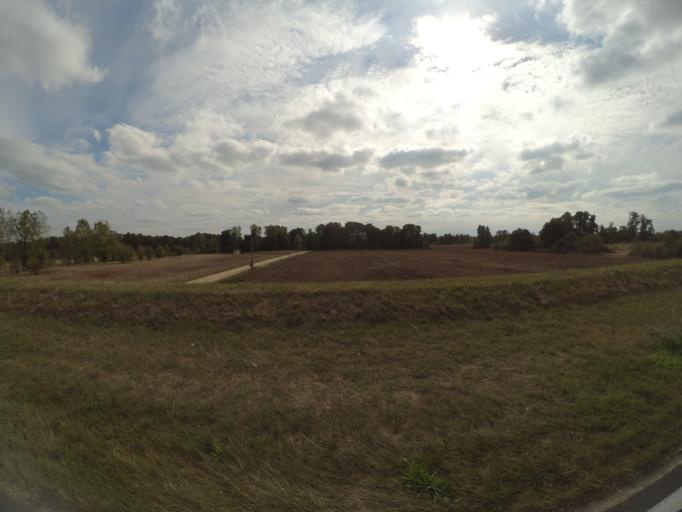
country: FR
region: Centre
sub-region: Departement d'Indre-et-Loire
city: Fondettes
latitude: 47.3829
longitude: 0.5814
